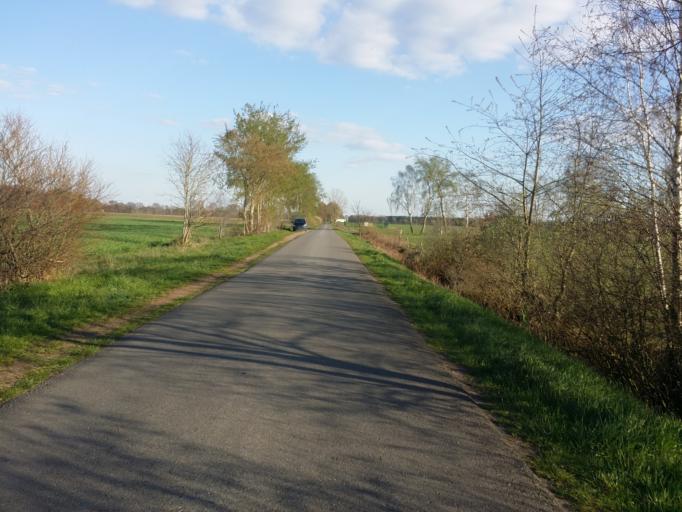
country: DE
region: Lower Saxony
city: Delmenhorst
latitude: 53.0112
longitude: 8.6314
